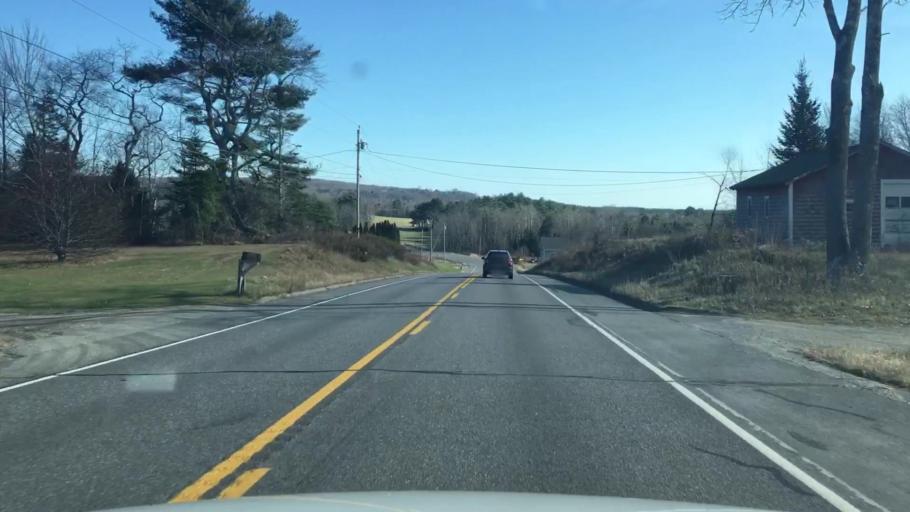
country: US
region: Maine
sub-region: Knox County
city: Washington
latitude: 44.2404
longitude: -69.3677
